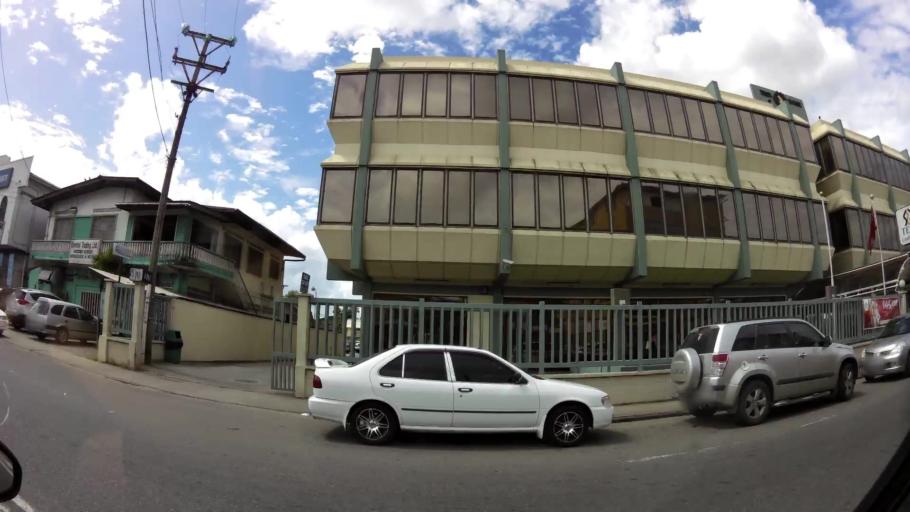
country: TT
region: City of San Fernando
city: Marabella
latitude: 10.3079
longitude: -61.4521
